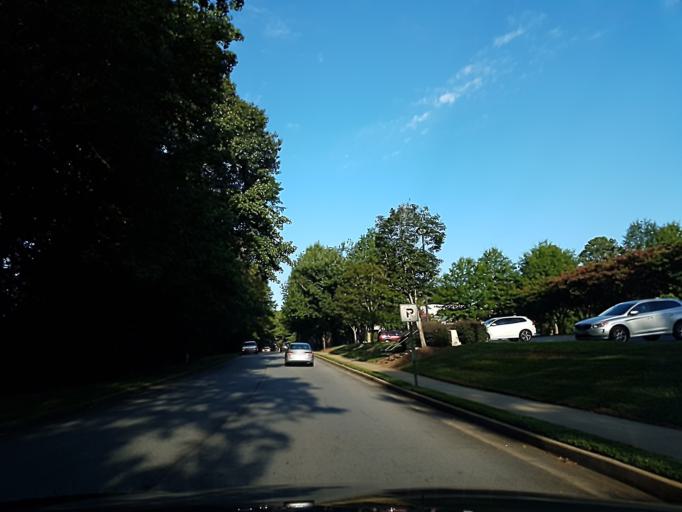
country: US
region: Georgia
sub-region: DeKalb County
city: Doraville
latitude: 33.8760
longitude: -84.2699
